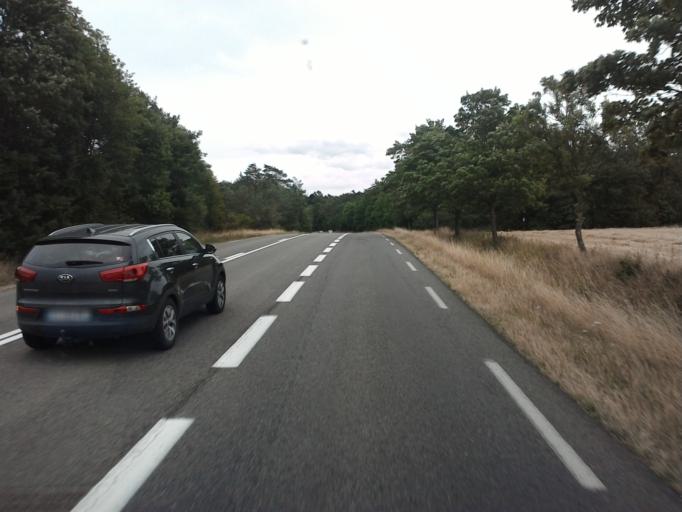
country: FR
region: Lorraine
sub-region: Departement de Meurthe-et-Moselle
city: Colombey-les-Belles
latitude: 48.5755
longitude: 5.9869
